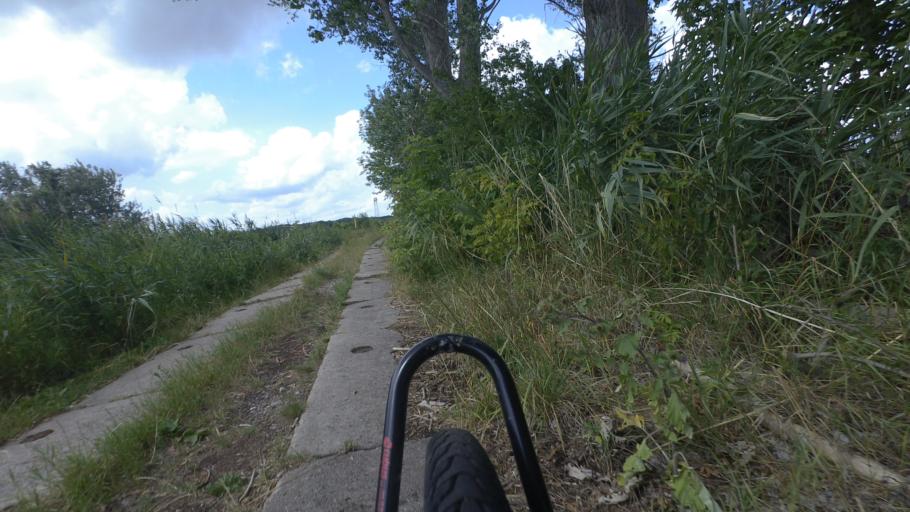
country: DE
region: Brandenburg
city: Grossbeeren
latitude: 52.3094
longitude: 13.3451
